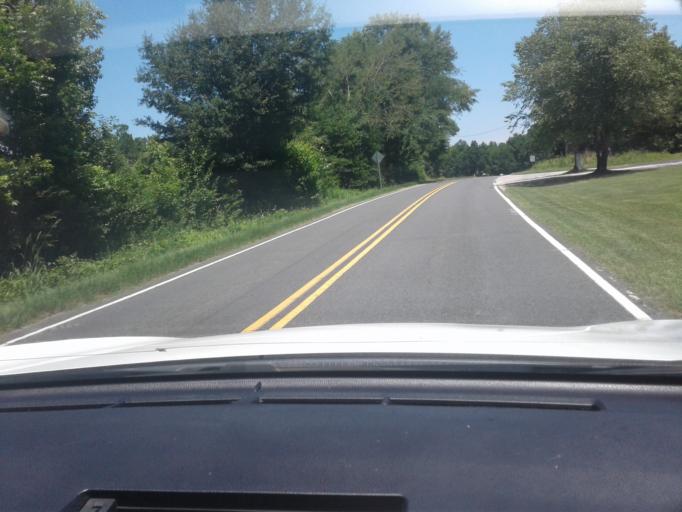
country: US
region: North Carolina
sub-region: Harnett County
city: Lillington
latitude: 35.3897
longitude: -78.7923
